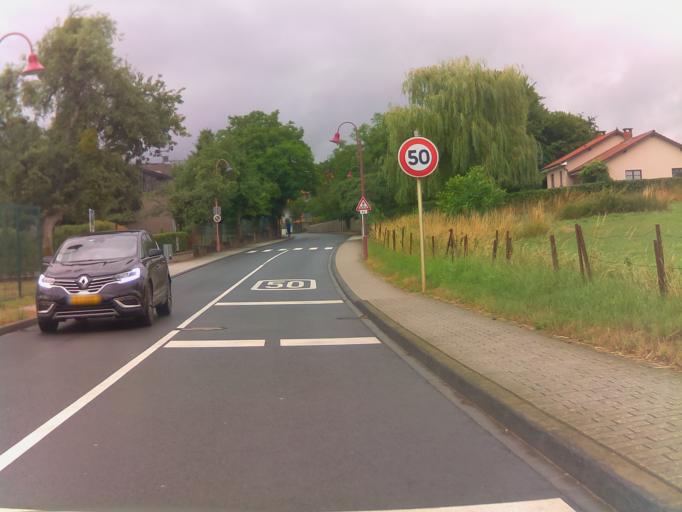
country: LU
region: Grevenmacher
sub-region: Canton de Remich
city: Dalheim
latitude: 49.5319
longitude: 6.2511
